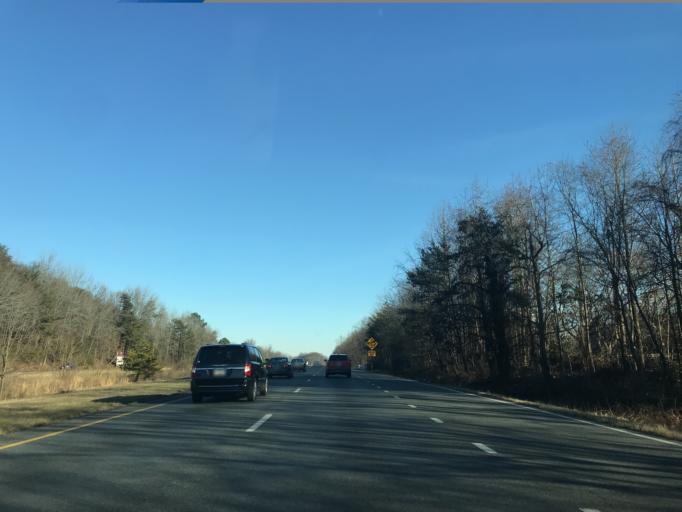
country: US
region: Maryland
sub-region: Prince George's County
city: Mellwood
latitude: 38.8188
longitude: -76.8441
